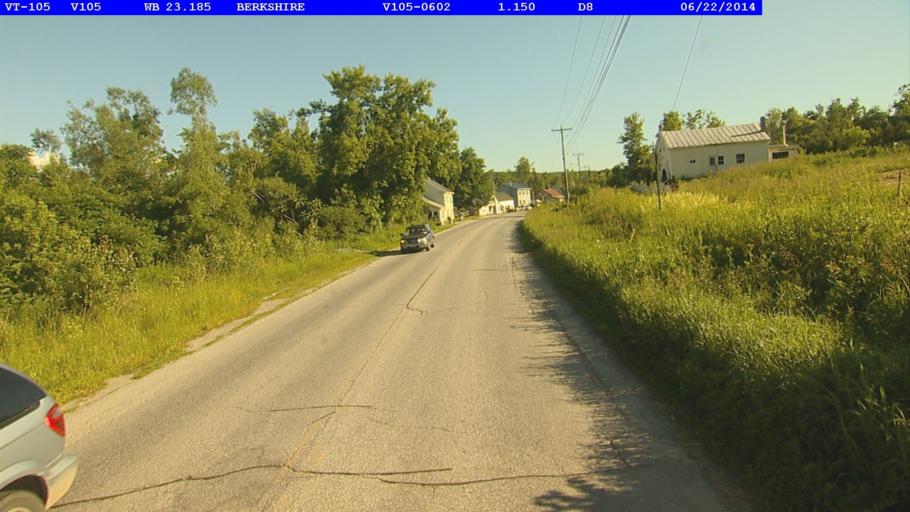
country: US
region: Vermont
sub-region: Franklin County
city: Richford
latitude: 44.9370
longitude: -72.7083
